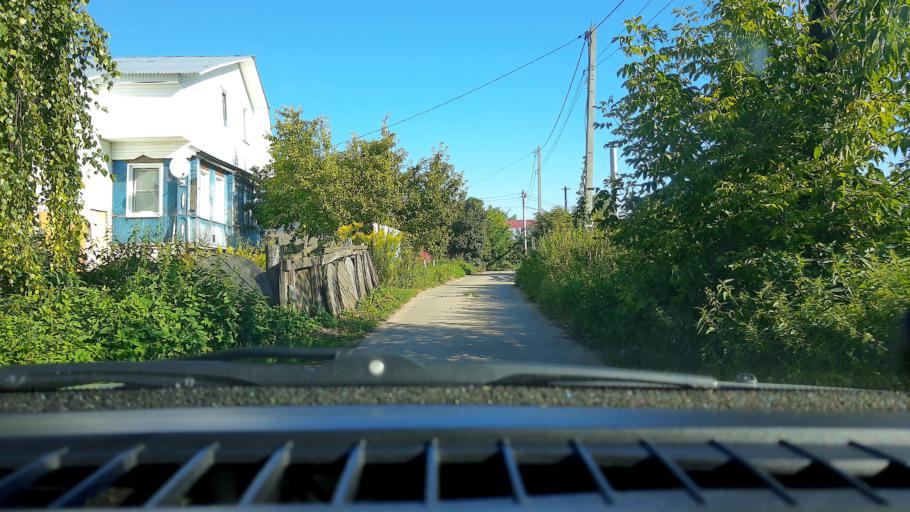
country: RU
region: Nizjnij Novgorod
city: Afonino
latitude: 56.2995
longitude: 44.0997
